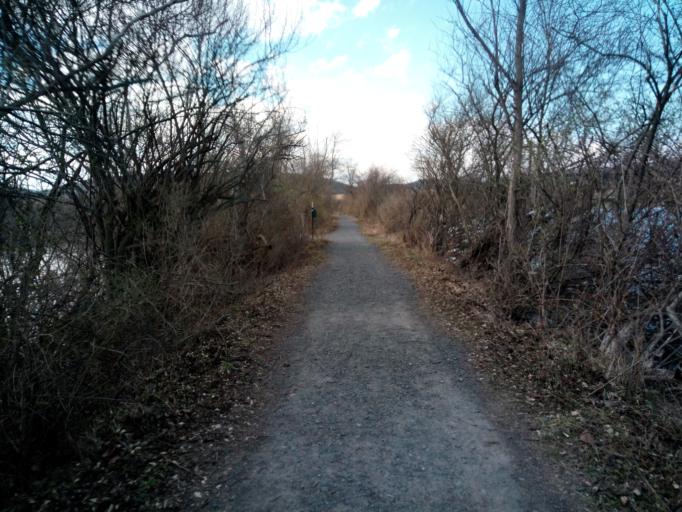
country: US
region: New York
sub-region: Chemung County
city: Big Flats
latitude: 42.1453
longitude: -76.9121
